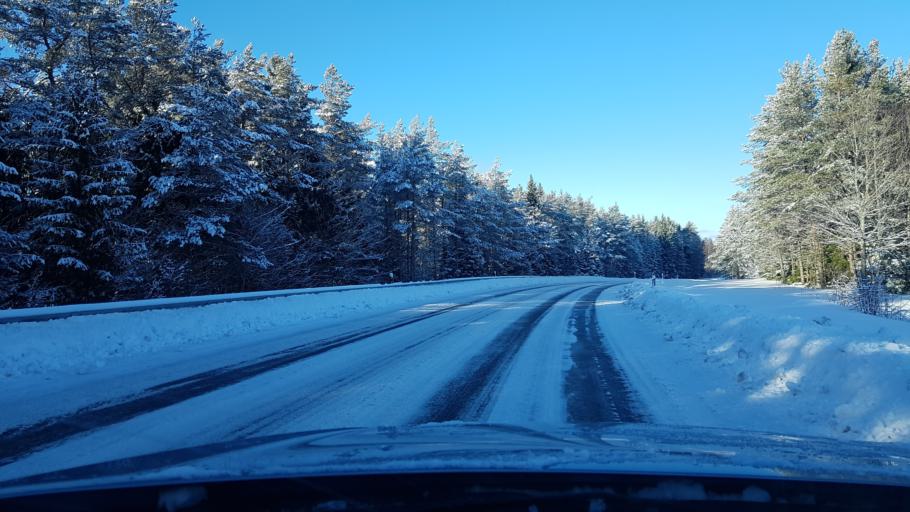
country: EE
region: Hiiumaa
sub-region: Kaerdla linn
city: Kardla
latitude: 58.9744
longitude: 22.7630
